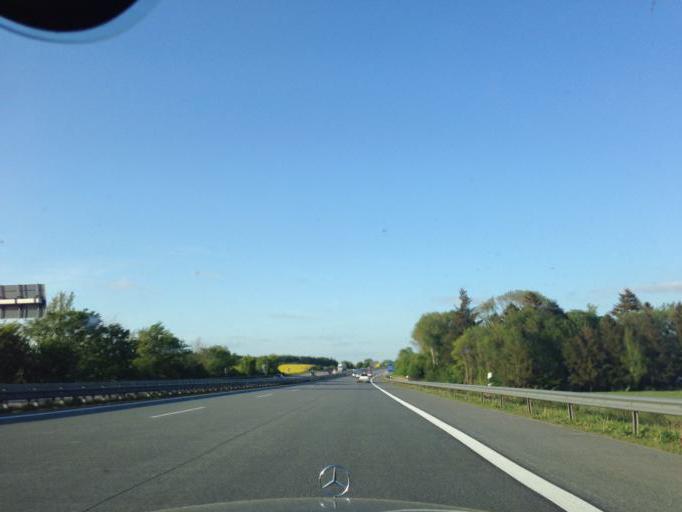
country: DE
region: Schleswig-Holstein
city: Politz
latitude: 53.7871
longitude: 10.4213
